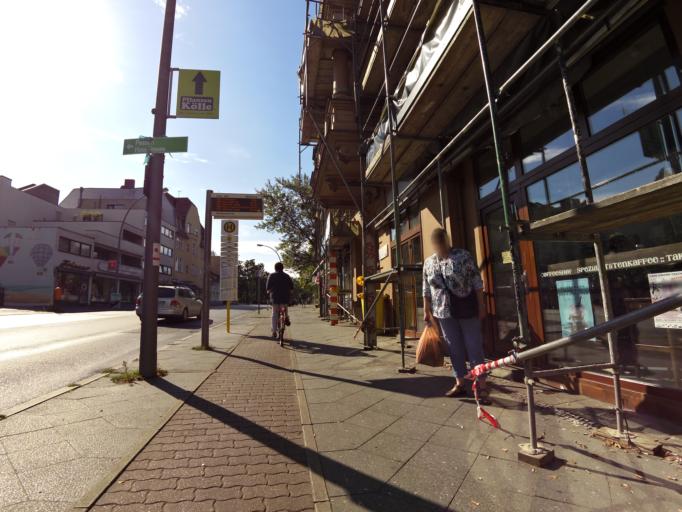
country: DE
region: Berlin
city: Zehlendorf Bezirk
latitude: 52.4303
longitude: 13.2593
